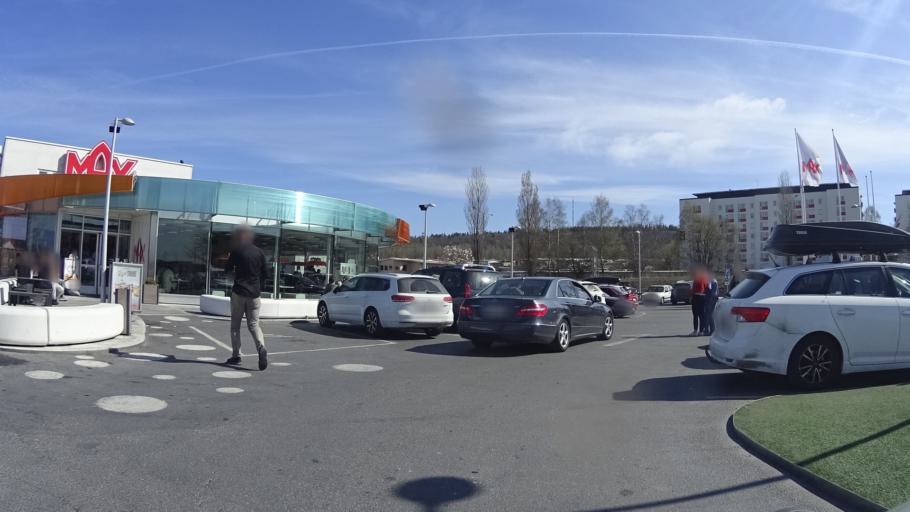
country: SE
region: Joenkoeping
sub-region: Jonkopings Kommun
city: Jonkoping
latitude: 57.7807
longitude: 14.2264
